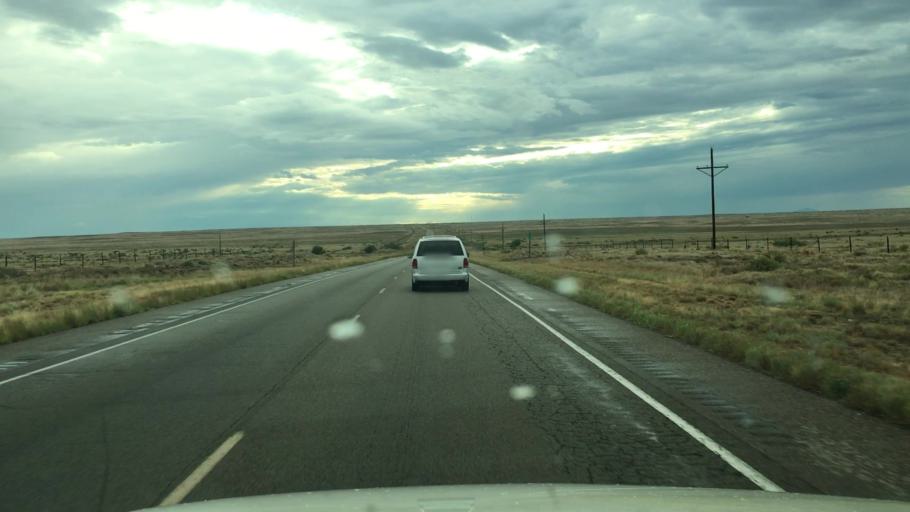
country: US
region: New Mexico
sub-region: Chaves County
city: Dexter
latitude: 33.4072
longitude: -104.2960
